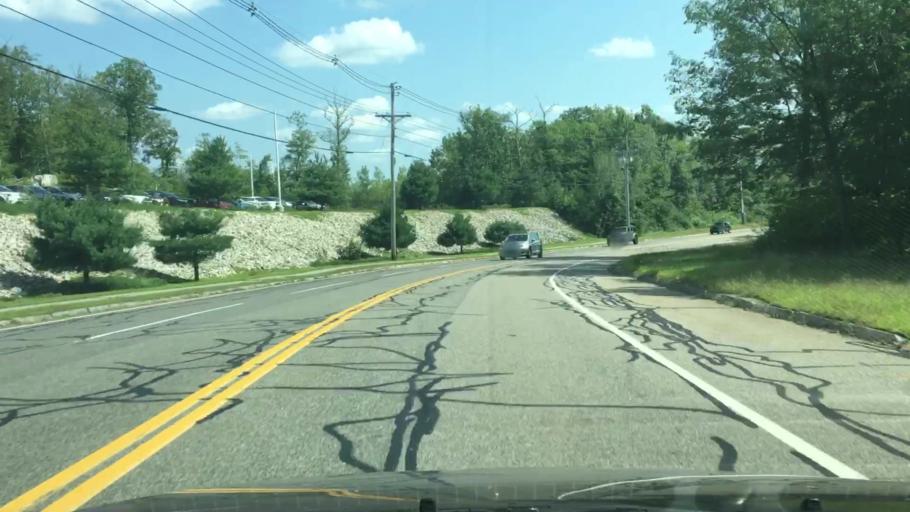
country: US
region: Massachusetts
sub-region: Worcester County
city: Milford
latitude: 42.1578
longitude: -71.4941
